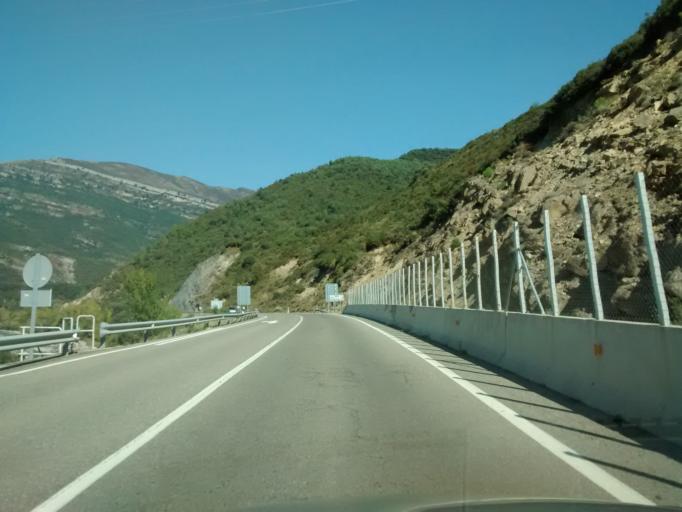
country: ES
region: Aragon
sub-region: Provincia de Huesca
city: Boltana
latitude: 42.4518
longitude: 0.0569
